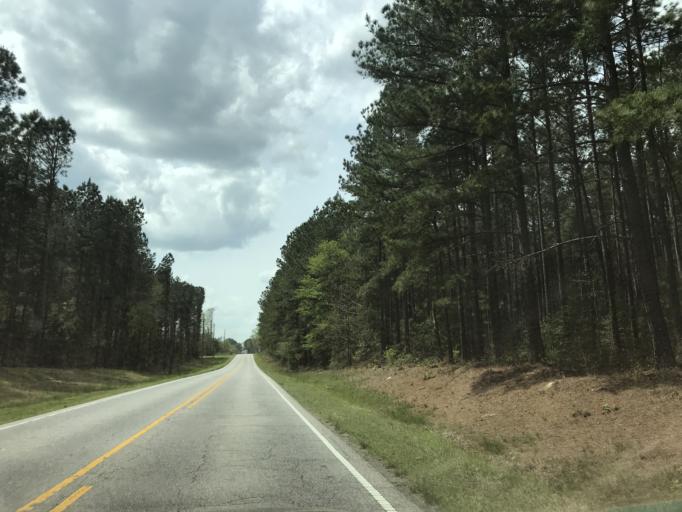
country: US
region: North Carolina
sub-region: Nash County
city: Spring Hope
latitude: 35.9634
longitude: -78.2426
